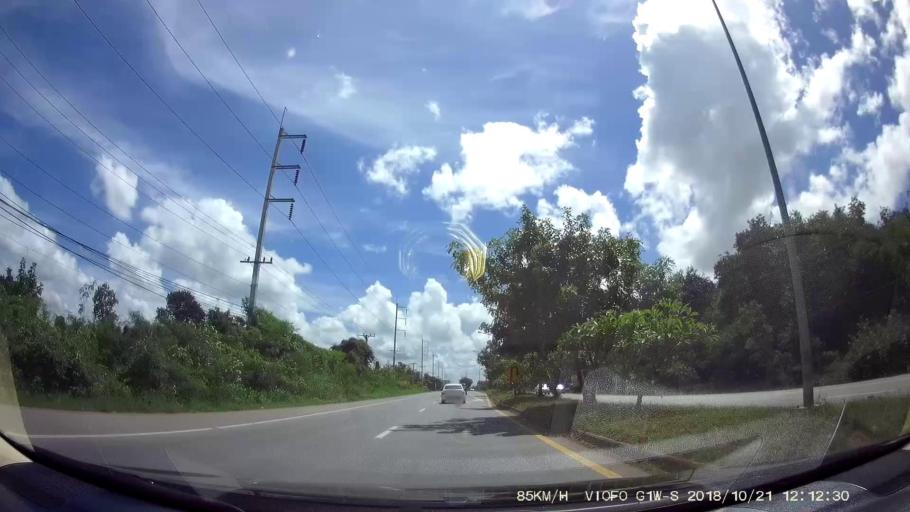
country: TH
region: Chaiyaphum
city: Chatturat
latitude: 15.4061
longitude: 101.8352
